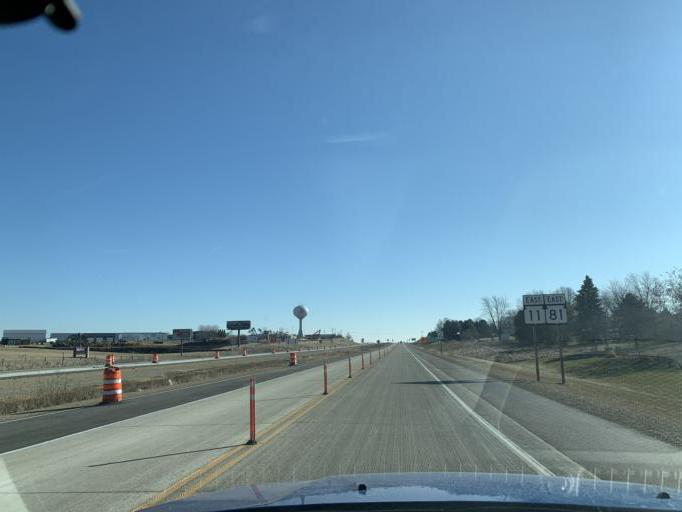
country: US
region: Wisconsin
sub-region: Green County
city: Monroe
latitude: 42.6139
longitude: -89.6298
